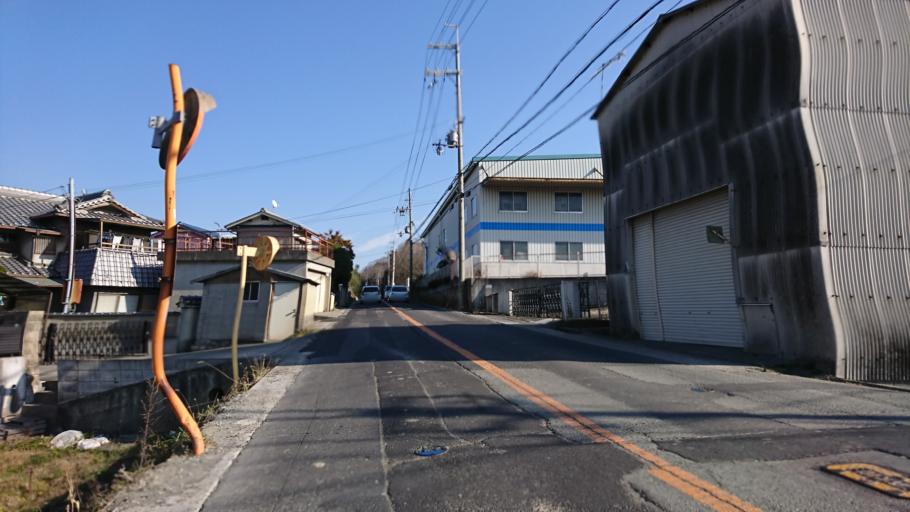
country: JP
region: Hyogo
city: Kakogawacho-honmachi
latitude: 34.8140
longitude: 134.8383
